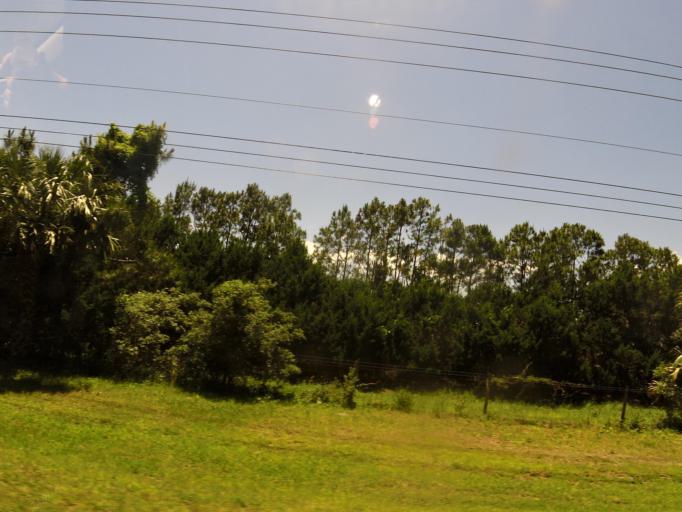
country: US
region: Florida
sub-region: Flagler County
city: Flagler Beach
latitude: 29.4561
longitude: -81.1681
